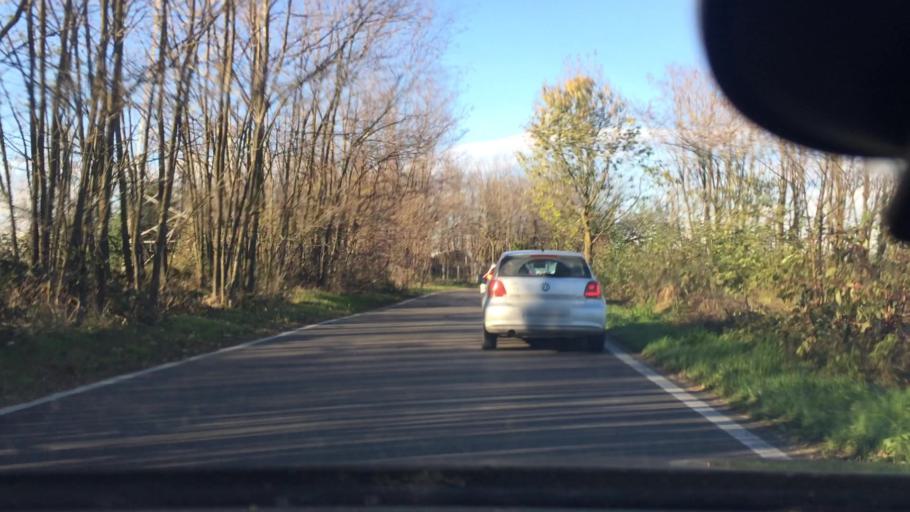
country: IT
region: Lombardy
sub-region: Citta metropolitana di Milano
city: Cerro Maggiore
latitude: 45.6049
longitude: 8.9523
